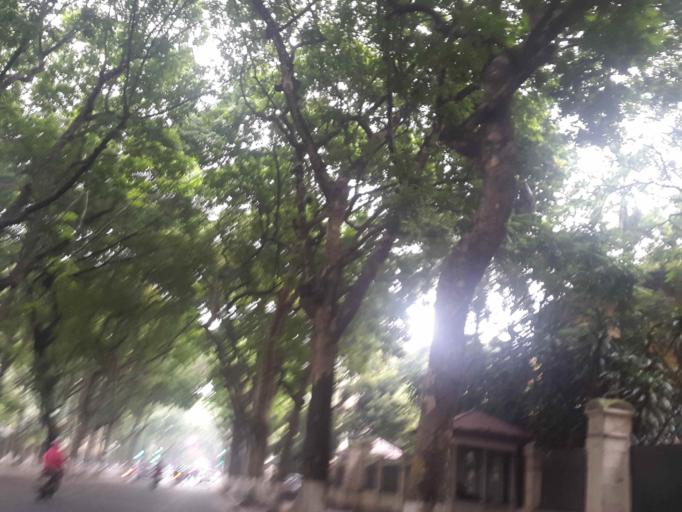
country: VN
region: Ha Noi
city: Hanoi
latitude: 21.0411
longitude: 105.8388
